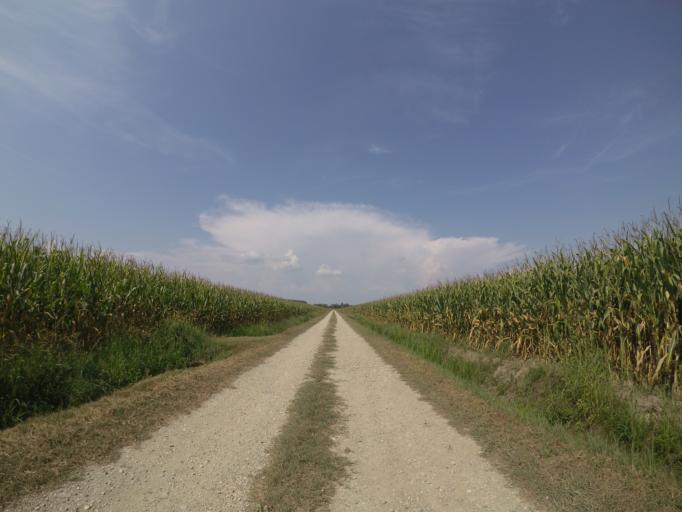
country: IT
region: Friuli Venezia Giulia
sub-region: Provincia di Udine
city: Varmo
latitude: 45.9161
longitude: 13.0175
